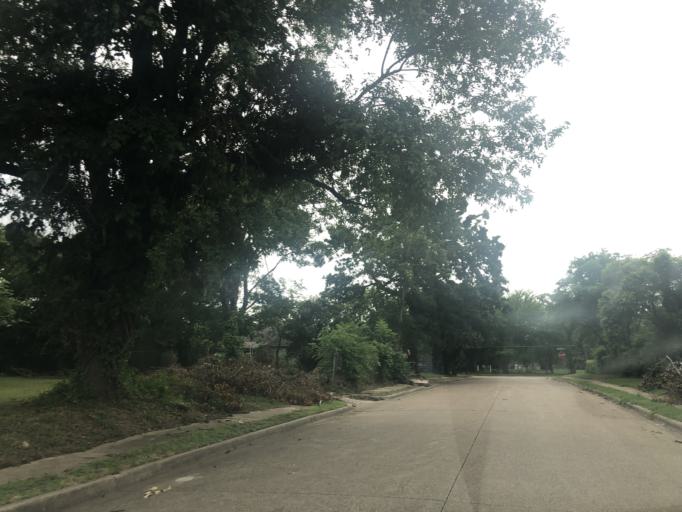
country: US
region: Texas
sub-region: Dallas County
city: Dallas
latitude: 32.7810
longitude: -96.8503
